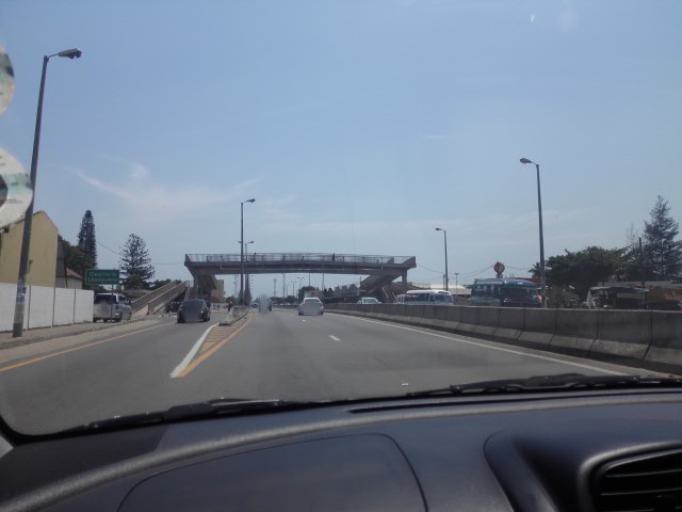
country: MZ
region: Maputo City
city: Maputo
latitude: -25.9405
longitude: 32.5448
